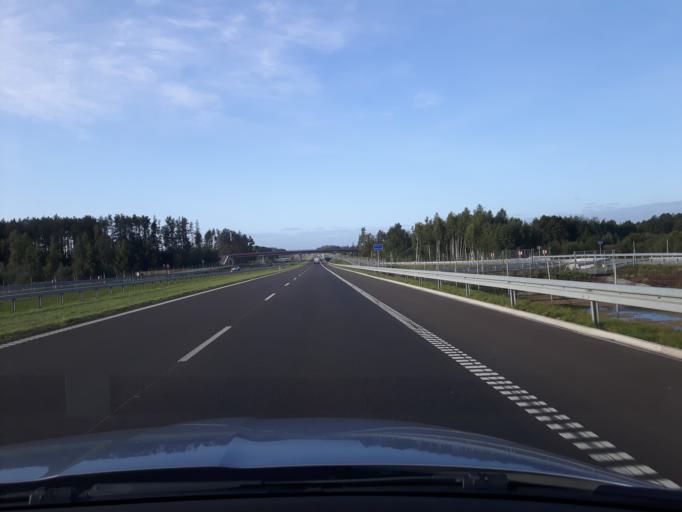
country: PL
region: Masovian Voivodeship
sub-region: Powiat radomski
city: Jedlinsk
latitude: 51.4912
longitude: 21.0717
